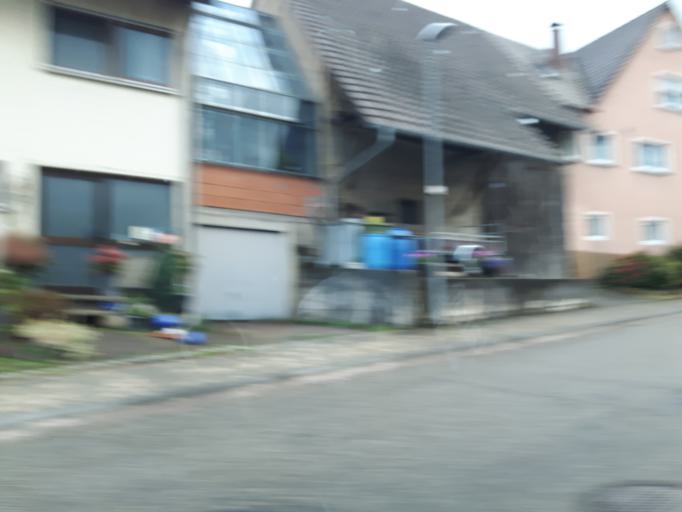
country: DE
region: Baden-Wuerttemberg
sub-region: Regierungsbezirk Stuttgart
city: Guglingen
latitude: 49.0486
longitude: 9.0002
